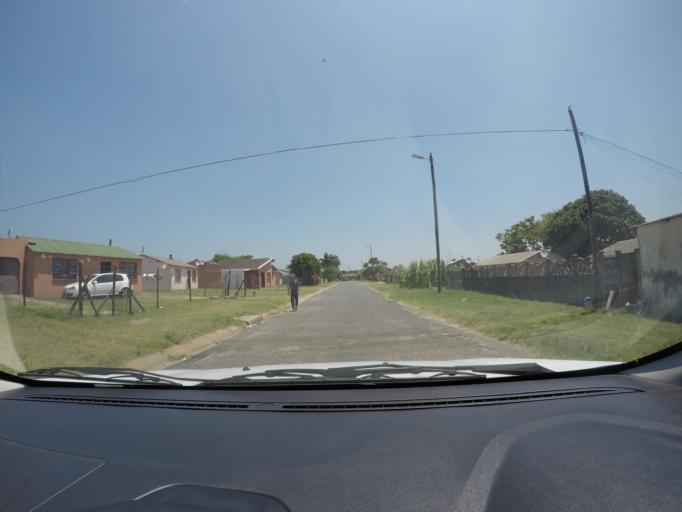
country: ZA
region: KwaZulu-Natal
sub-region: uThungulu District Municipality
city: eSikhawini
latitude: -28.8846
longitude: 31.8878
